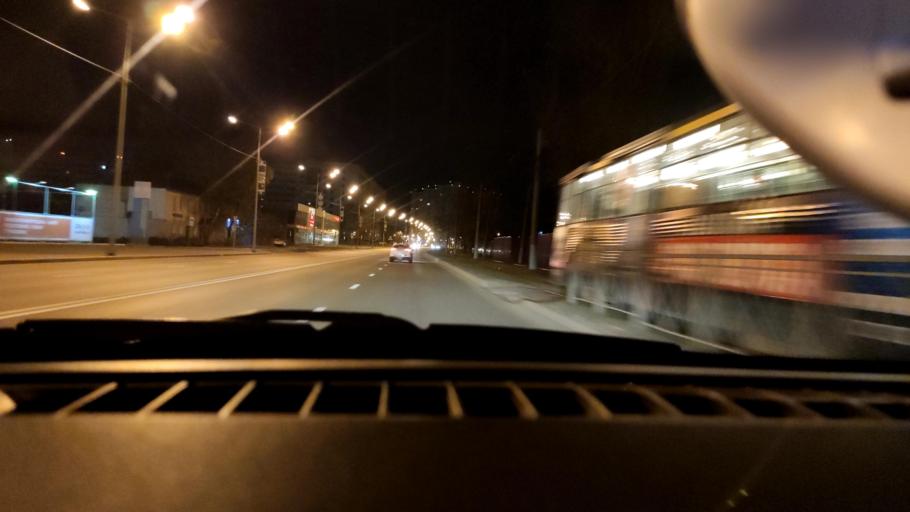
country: RU
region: Perm
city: Kondratovo
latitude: 57.9645
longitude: 56.1422
